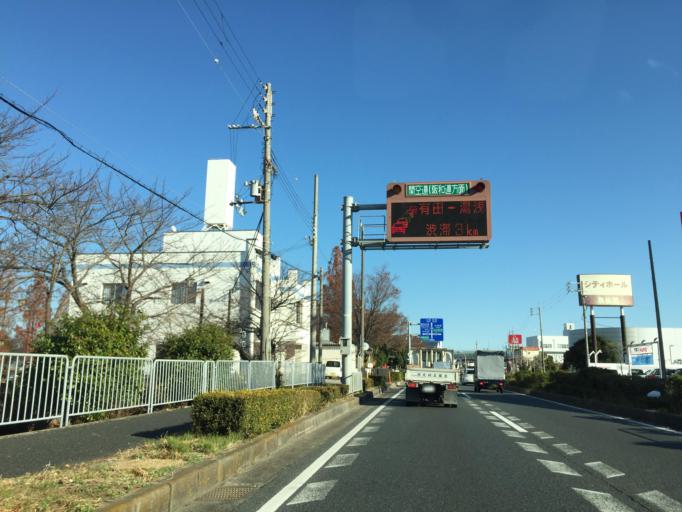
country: JP
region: Osaka
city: Kaizuka
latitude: 34.3979
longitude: 135.3092
